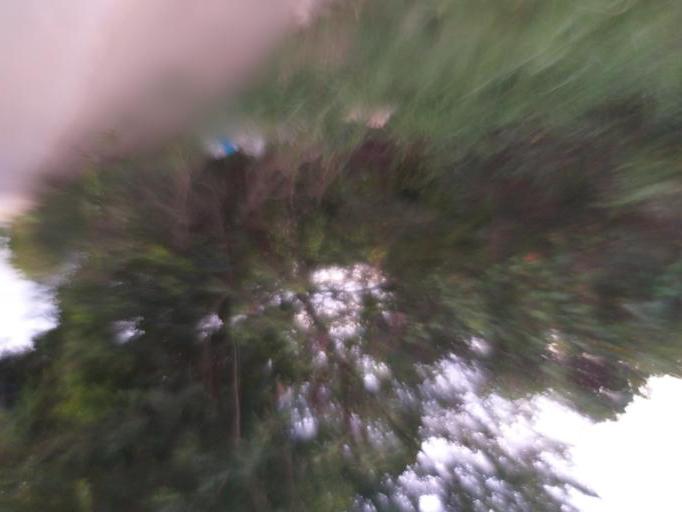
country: TH
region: Pathum Thani
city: Ban Lam Luk Ka
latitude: 14.0011
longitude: 100.8001
